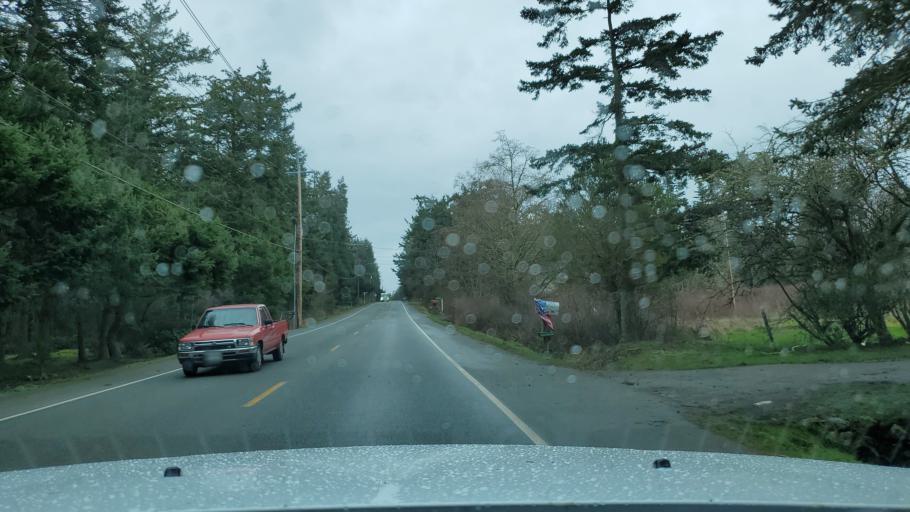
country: US
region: Washington
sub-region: Island County
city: Coupeville
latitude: 48.2731
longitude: -122.7370
